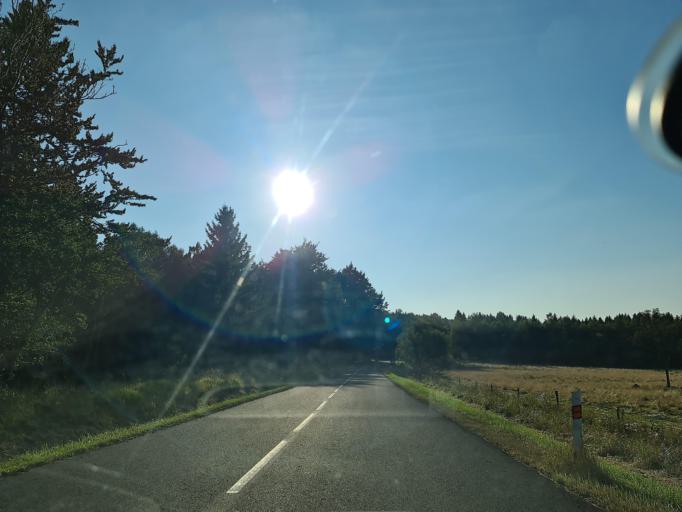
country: DE
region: Saxony
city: Deutschneudorf
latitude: 50.5895
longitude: 13.4776
